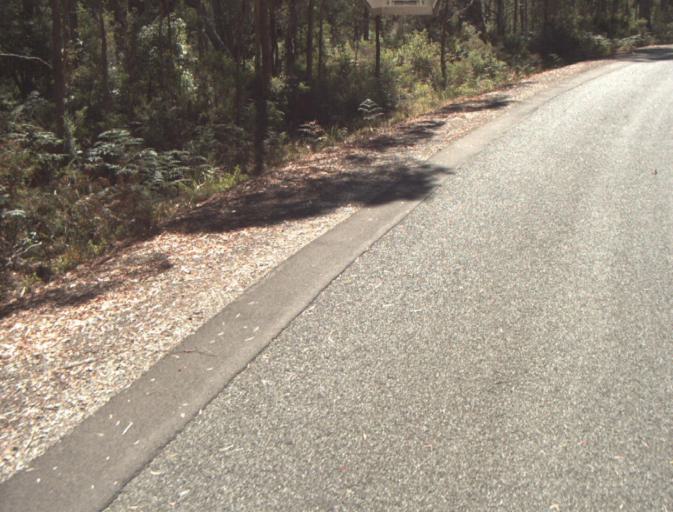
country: AU
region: Tasmania
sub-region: Launceston
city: Newstead
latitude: -41.3097
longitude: 147.3344
